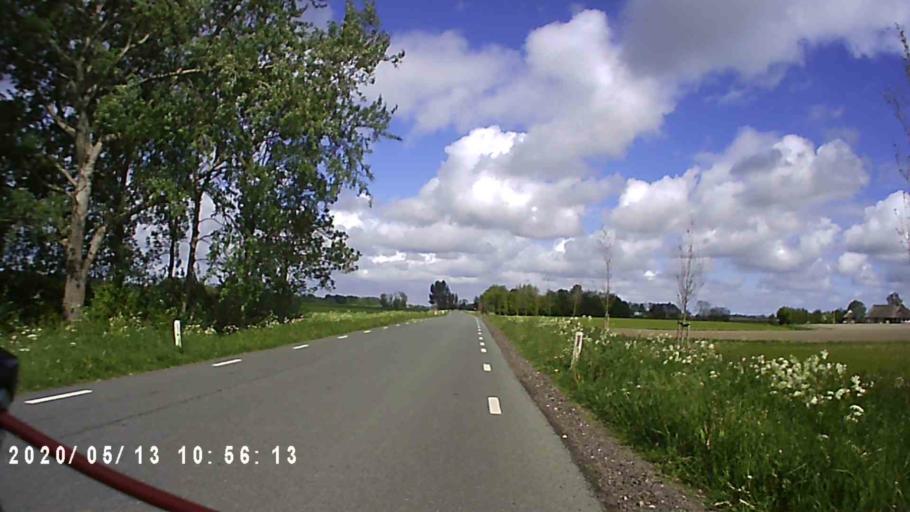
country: NL
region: Groningen
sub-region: Gemeente Zuidhorn
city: Grijpskerk
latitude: 53.2696
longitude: 6.3366
